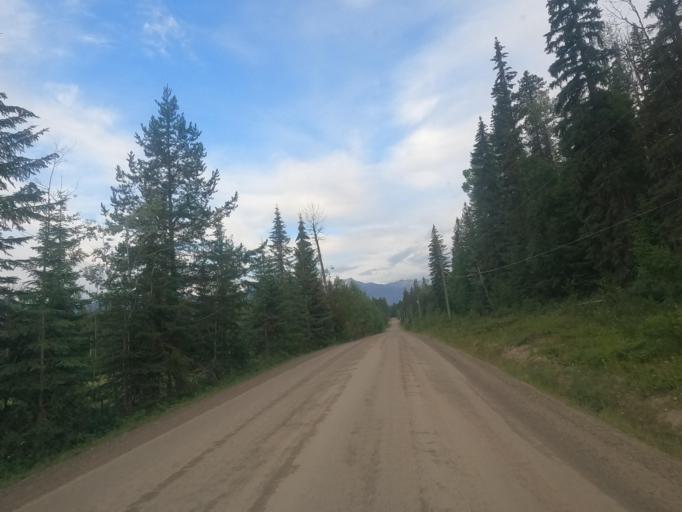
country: CA
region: British Columbia
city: Golden
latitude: 51.4385
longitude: -117.0480
